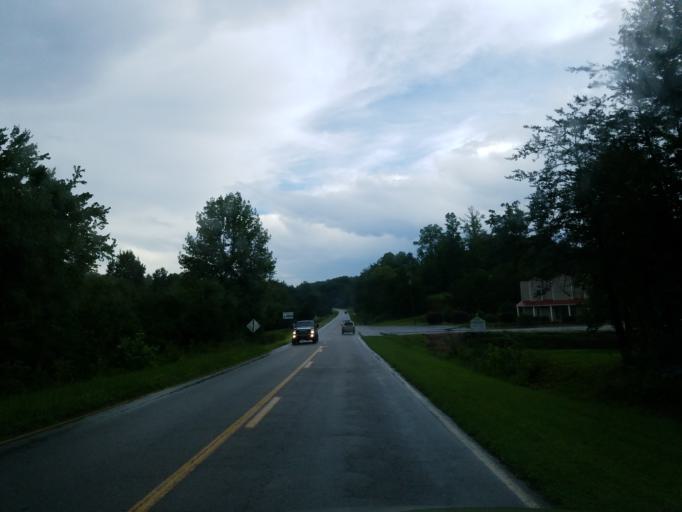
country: US
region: Georgia
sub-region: Lumpkin County
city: Dahlonega
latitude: 34.5259
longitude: -83.9075
